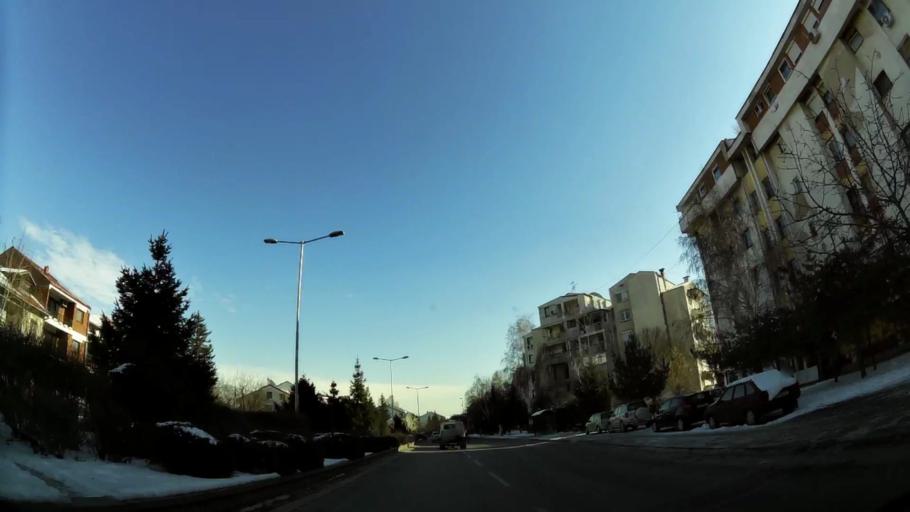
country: MK
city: Krushopek
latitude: 42.0063
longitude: 21.3689
